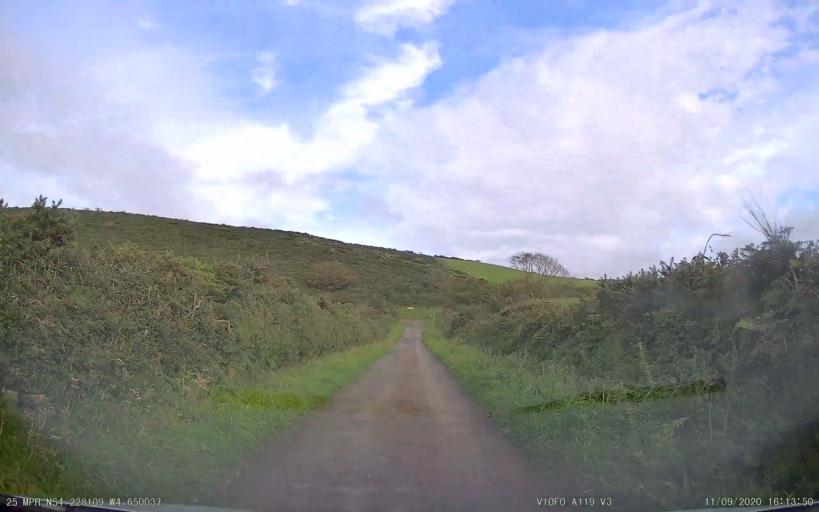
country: IM
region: Castletown
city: Castletown
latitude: 54.2281
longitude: -4.6500
